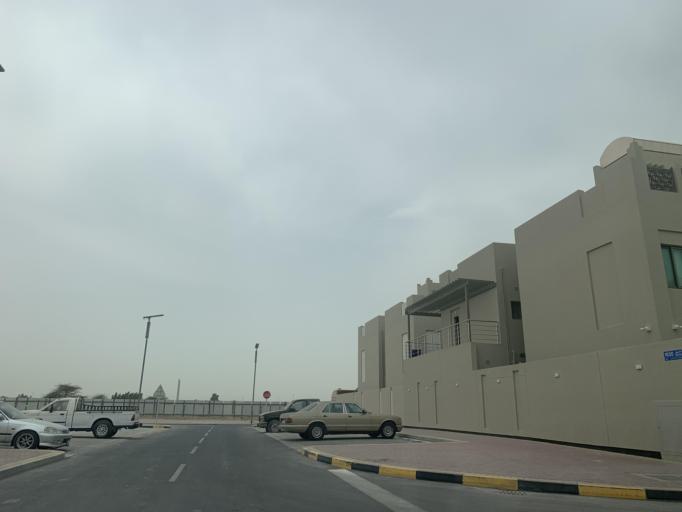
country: BH
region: Northern
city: Madinat `Isa
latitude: 26.1707
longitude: 50.5089
